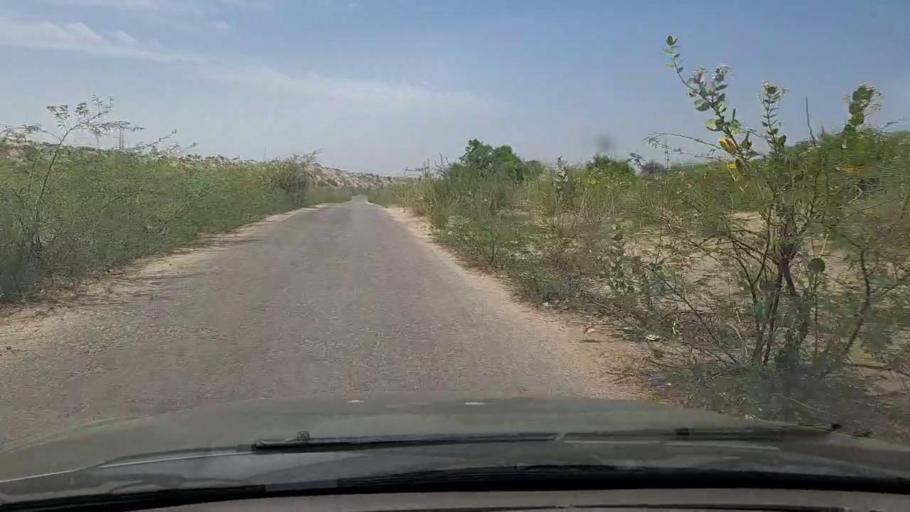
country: PK
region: Sindh
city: Diplo
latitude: 24.5368
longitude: 69.6409
